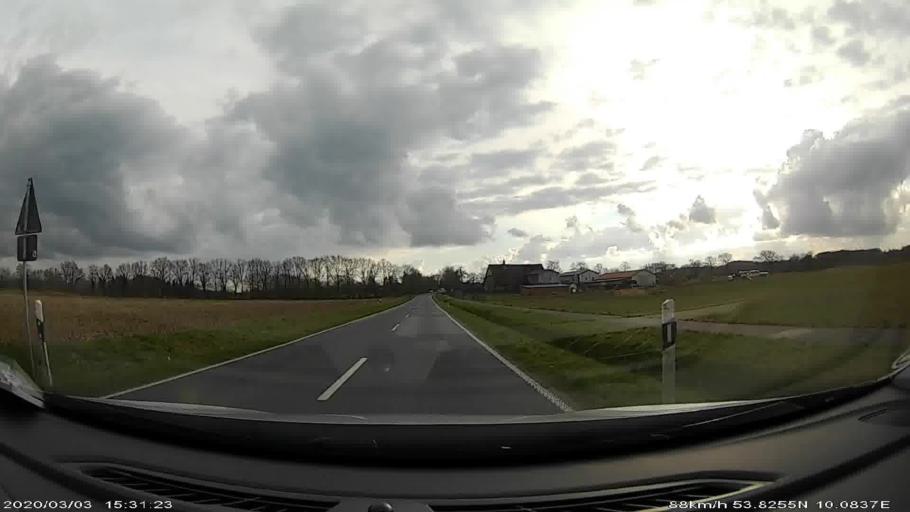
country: DE
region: Schleswig-Holstein
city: Huttblek
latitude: 53.8265
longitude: 10.0842
